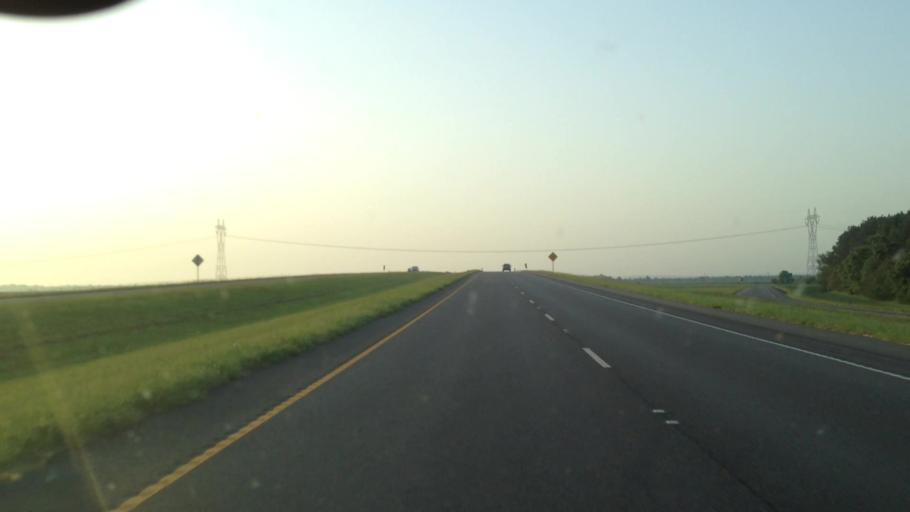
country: US
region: Louisiana
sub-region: Natchitoches Parish
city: Campti
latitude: 31.8402
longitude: -93.2812
